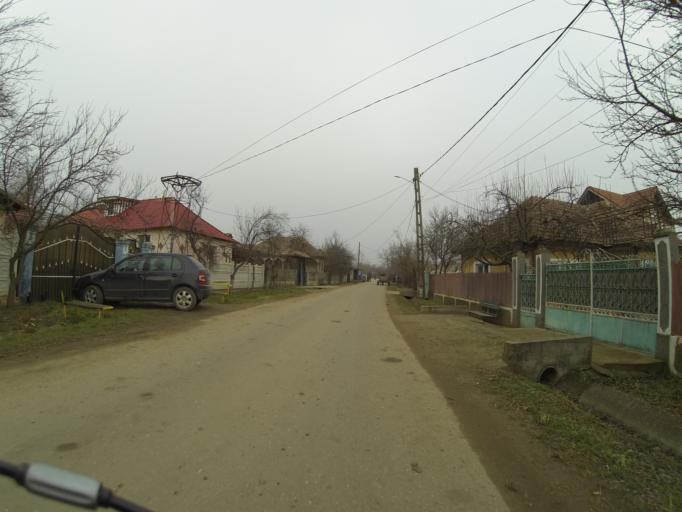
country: RO
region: Mehedinti
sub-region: Comuna Balacita
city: Gvardinita
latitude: 44.3968
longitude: 23.1445
